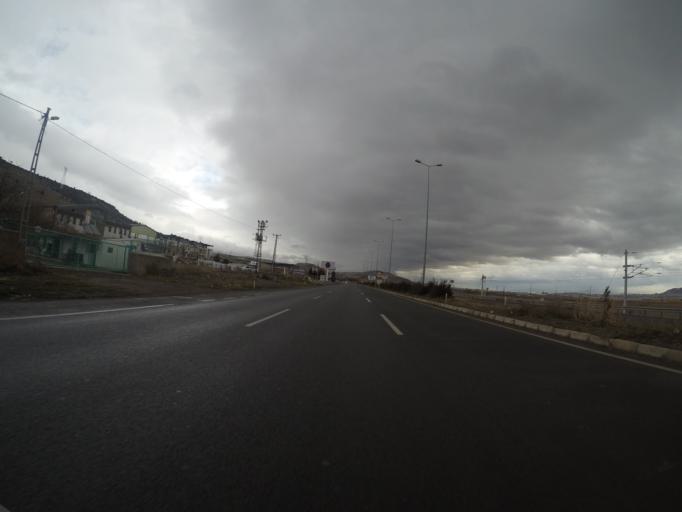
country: TR
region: Kayseri
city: Melikgazi
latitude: 38.7469
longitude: 35.3042
